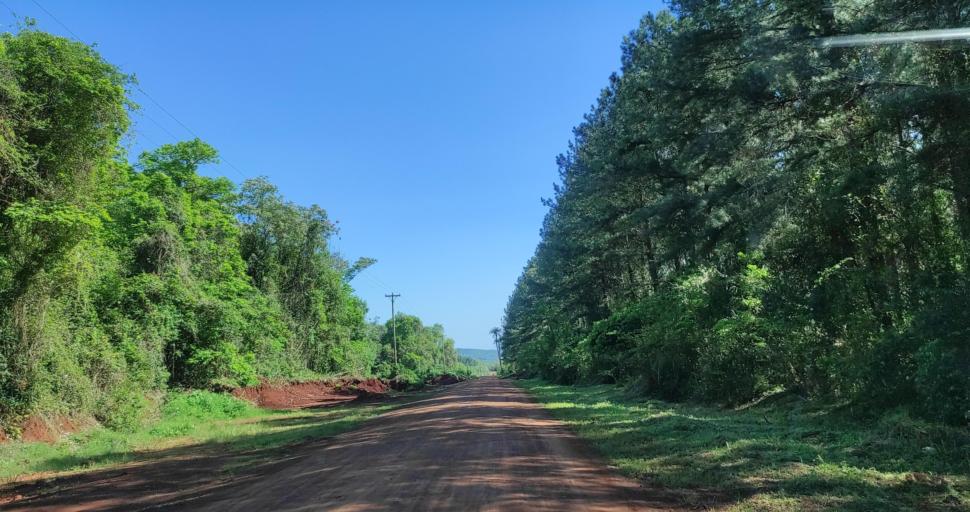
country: AR
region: Misiones
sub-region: Departamento de Candelaria
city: Loreto
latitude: -27.3286
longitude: -55.5250
